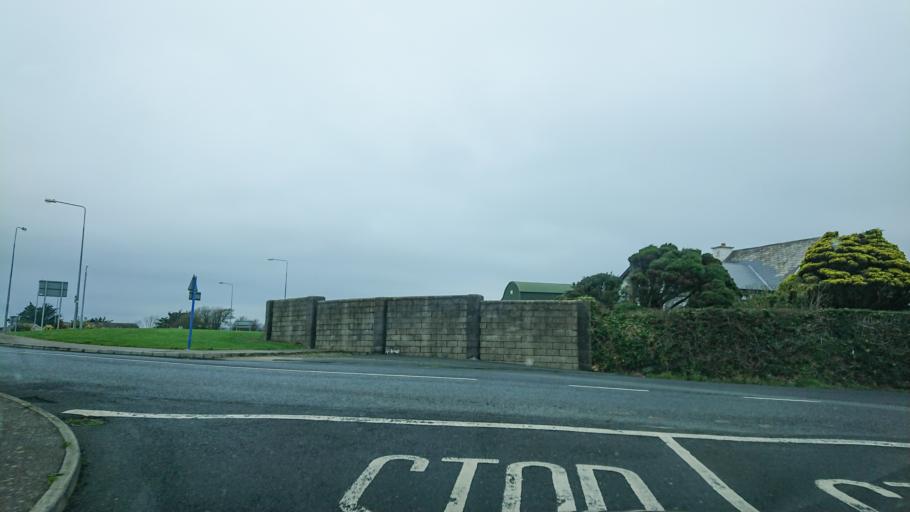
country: IE
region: Munster
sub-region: Waterford
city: Tra Mhor
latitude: 52.1538
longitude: -7.1685
